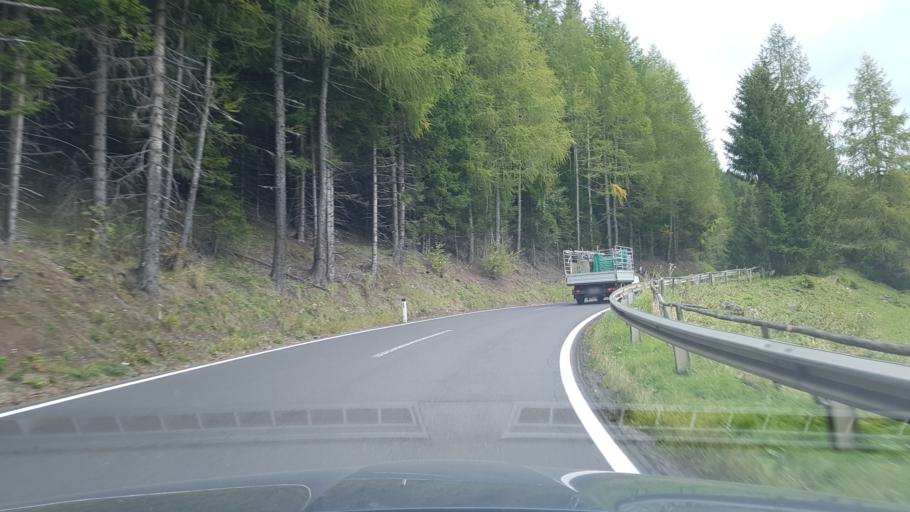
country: AT
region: Styria
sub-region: Politischer Bezirk Murtal
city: Kleinlobming
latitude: 47.1258
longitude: 14.8857
